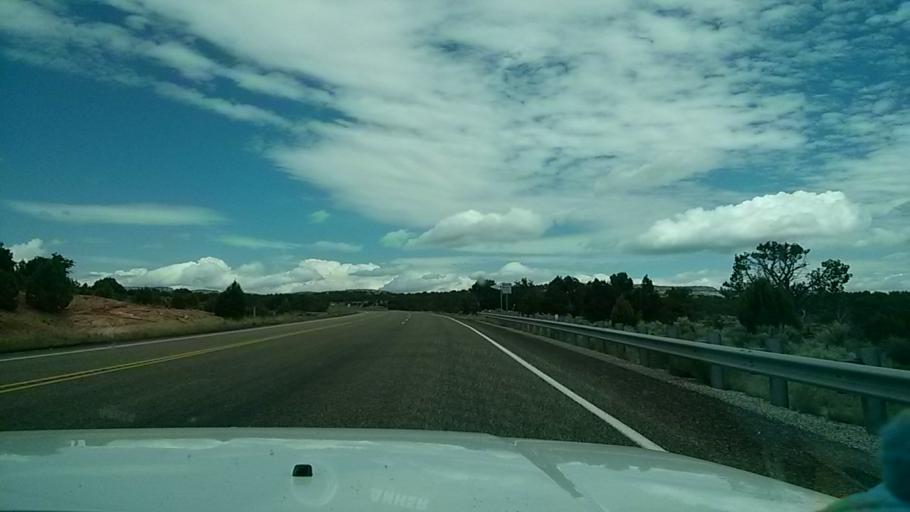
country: US
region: Utah
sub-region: Kane County
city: Kanab
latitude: 37.1490
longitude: -112.5699
